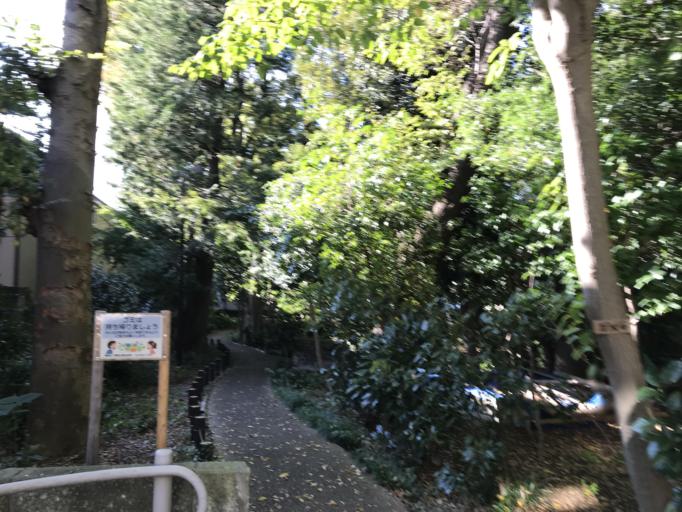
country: JP
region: Tokyo
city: Musashino
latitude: 35.7485
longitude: 139.5819
